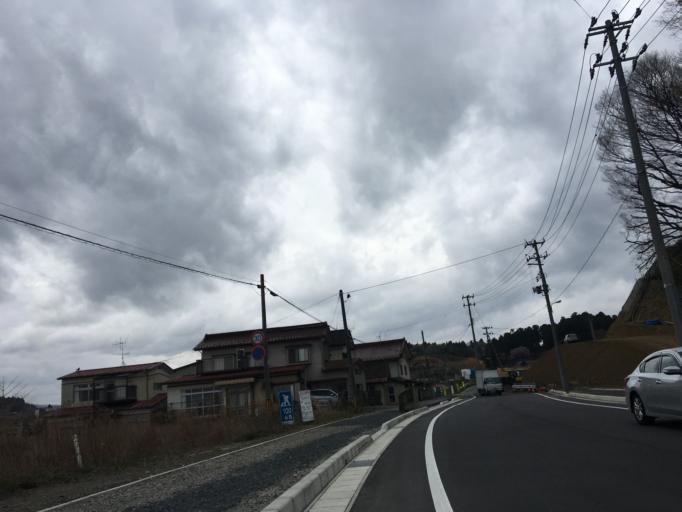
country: JP
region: Iwate
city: Ofunato
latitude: 38.8981
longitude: 141.5697
